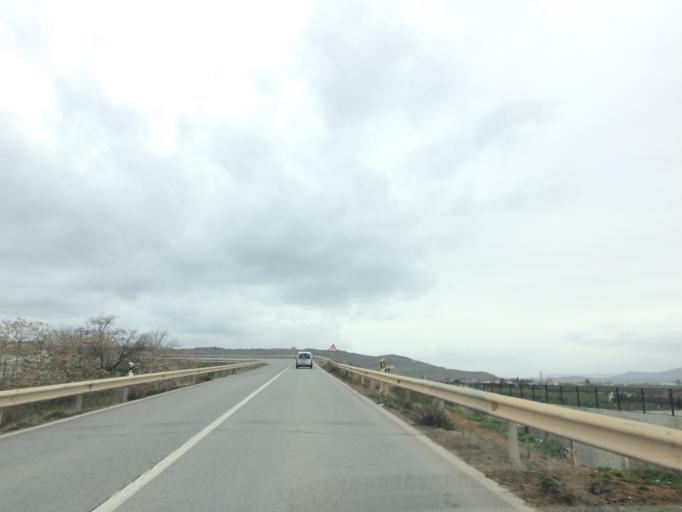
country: ES
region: Andalusia
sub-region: Provincia de Malaga
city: Antequera
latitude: 37.0289
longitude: -4.5621
